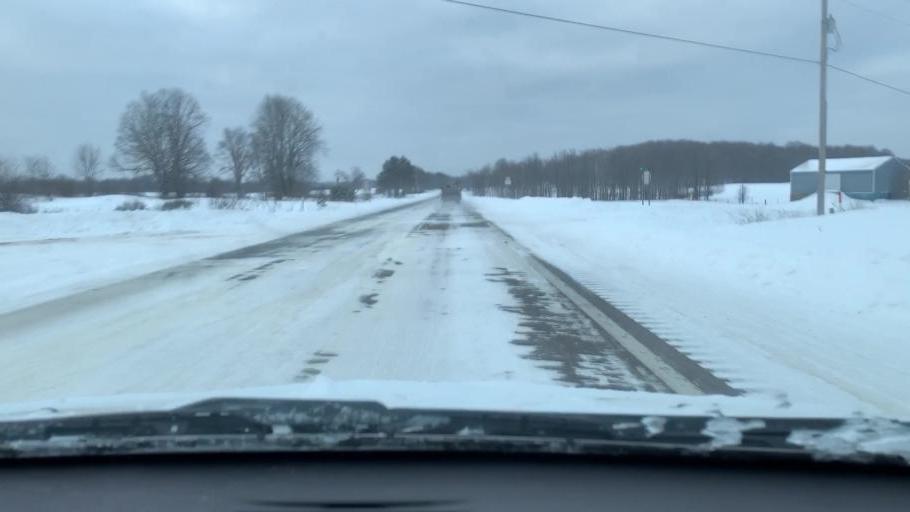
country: US
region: Michigan
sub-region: Wexford County
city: Manton
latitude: 44.5985
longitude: -85.3302
